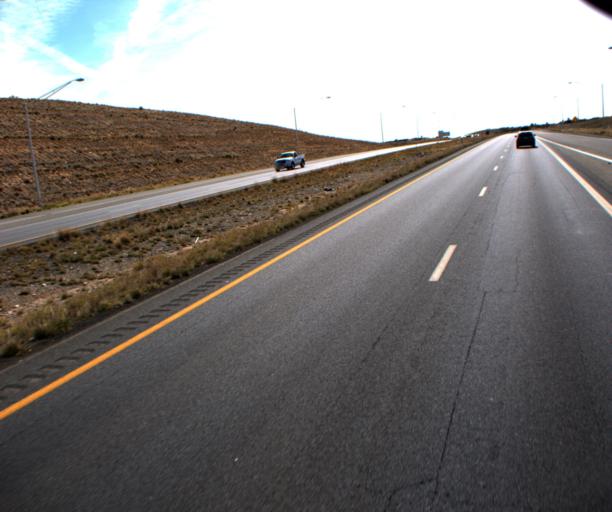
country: US
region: Arizona
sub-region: Yavapai County
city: Prescott Valley
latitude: 34.6340
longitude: -112.3942
